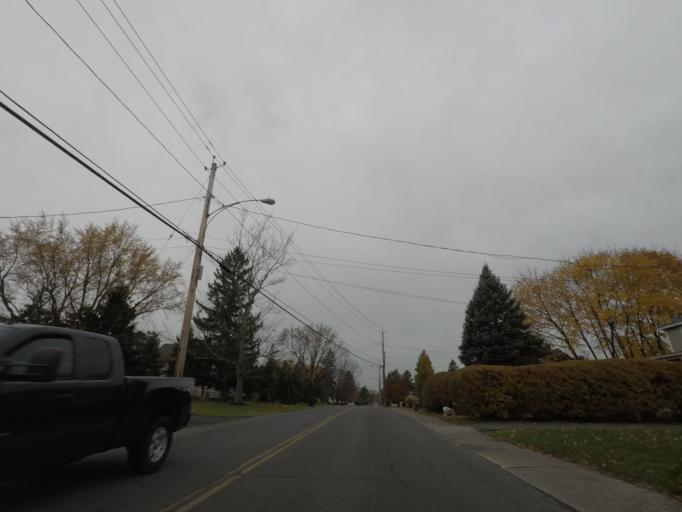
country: US
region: New York
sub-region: Albany County
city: Cohoes
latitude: 42.7857
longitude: -73.7237
